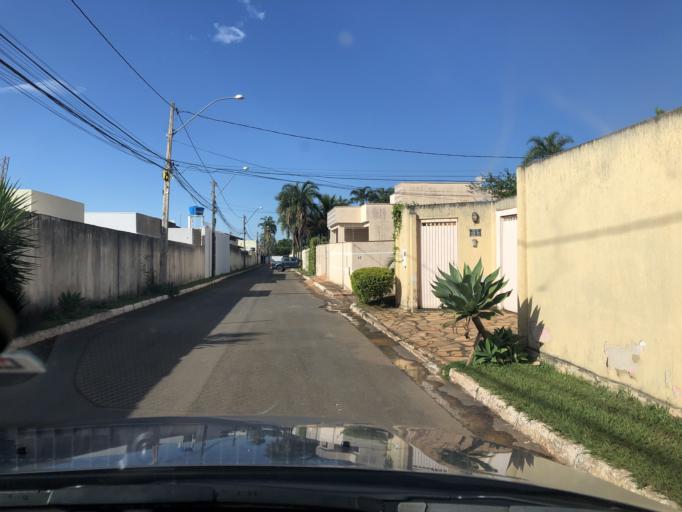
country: BR
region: Federal District
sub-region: Brasilia
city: Brasilia
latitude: -15.7980
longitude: -48.0362
